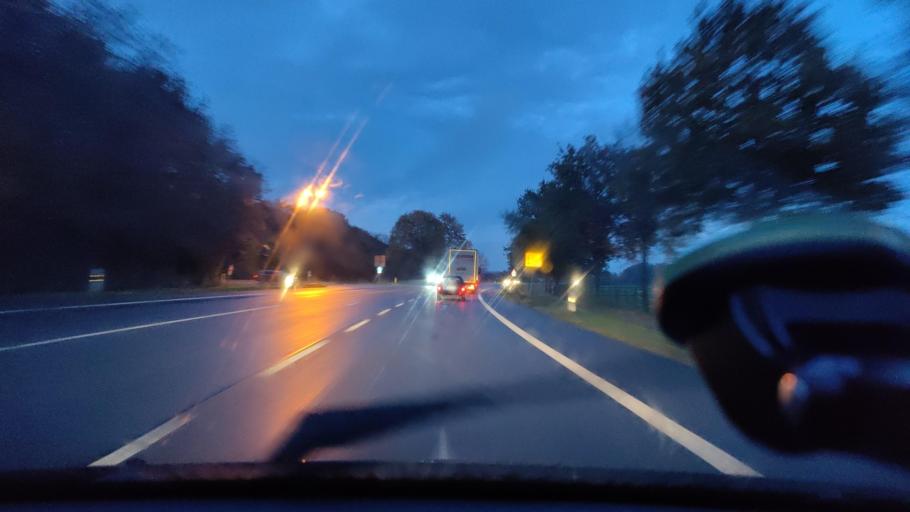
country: DE
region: North Rhine-Westphalia
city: Straelen
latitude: 51.4215
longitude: 6.2645
